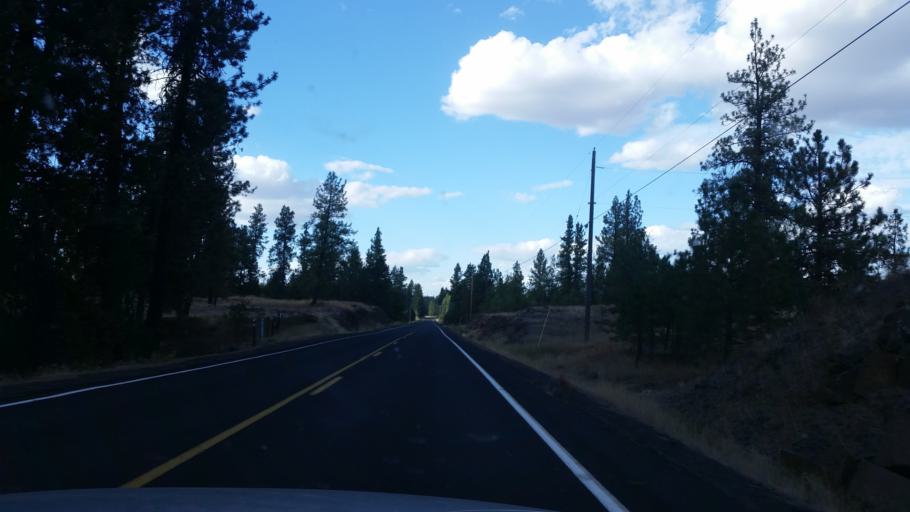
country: US
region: Washington
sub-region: Spokane County
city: Cheney
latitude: 47.4671
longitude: -117.5813
